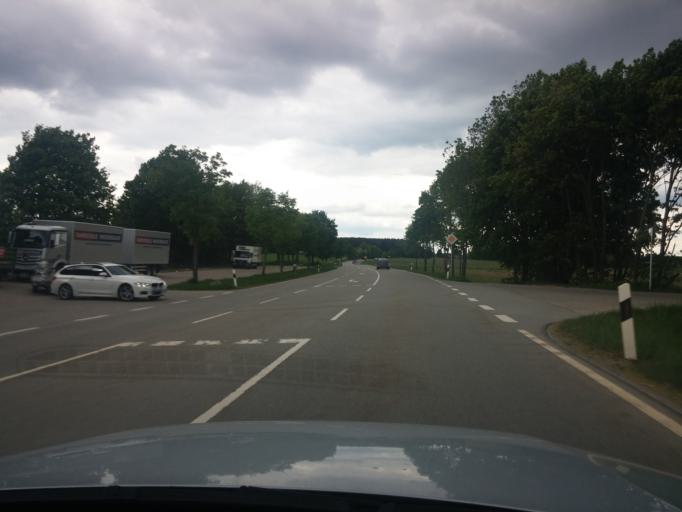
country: DE
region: Bavaria
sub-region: Upper Bavaria
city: Holzkirchen
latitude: 47.8606
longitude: 11.6893
